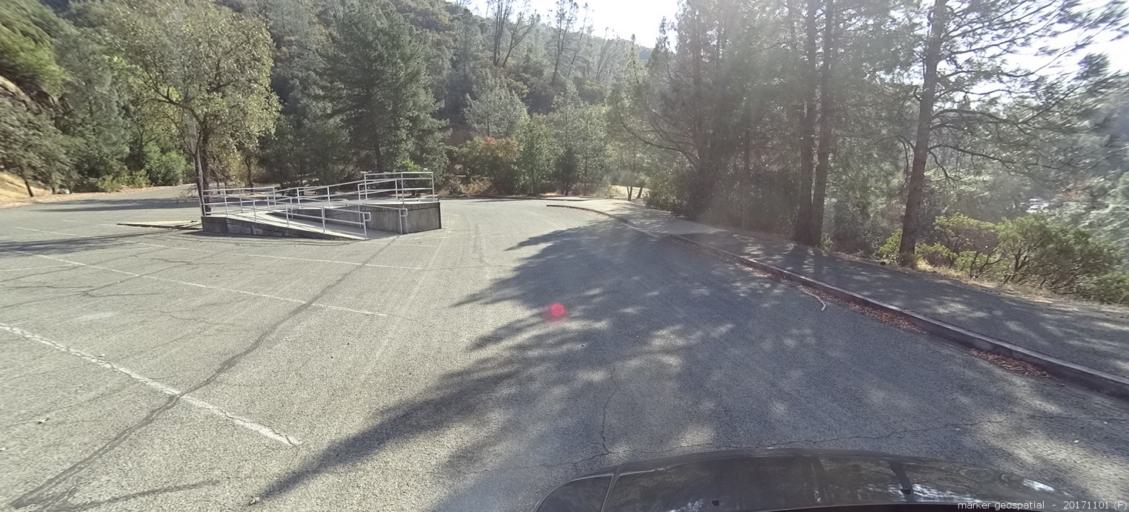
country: US
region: California
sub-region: Shasta County
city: Central Valley (historical)
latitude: 40.7166
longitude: -122.4058
